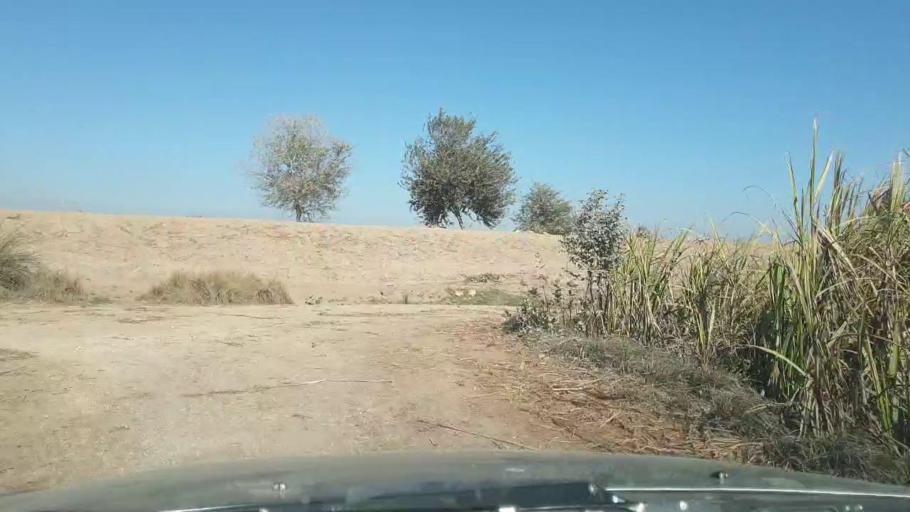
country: PK
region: Sindh
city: Ghotki
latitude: 28.0573
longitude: 69.2408
